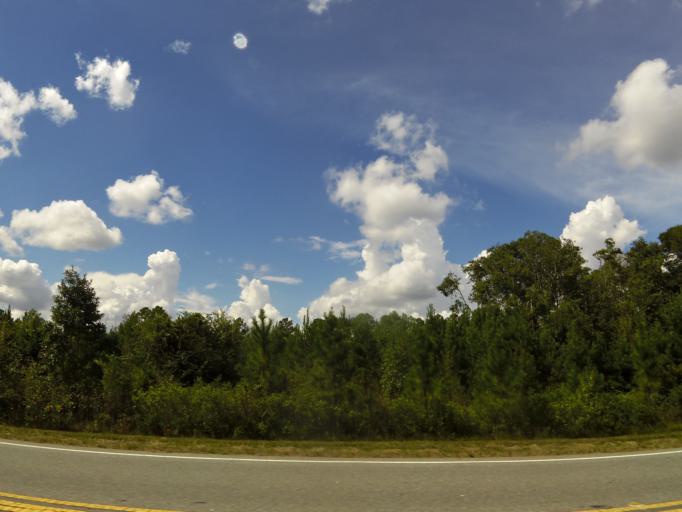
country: US
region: Georgia
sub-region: Brantley County
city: Nahunta
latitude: 31.0812
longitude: -82.0099
